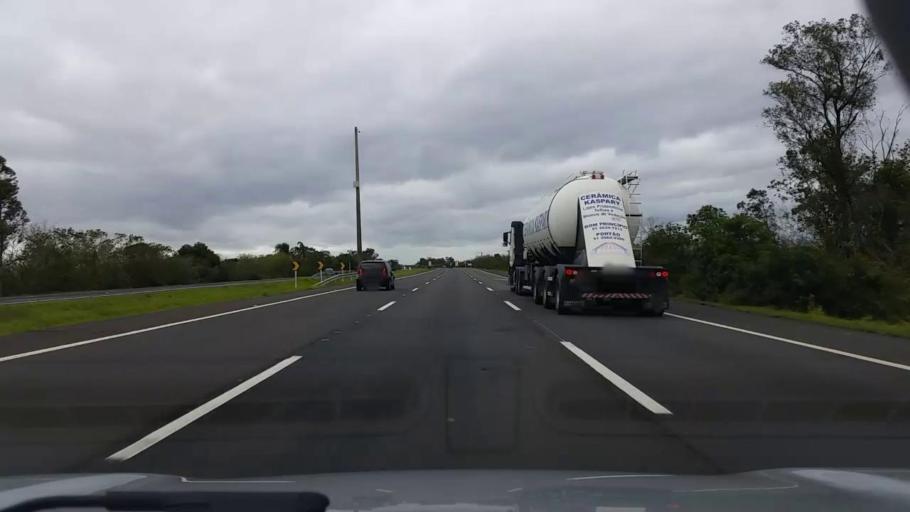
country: BR
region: Rio Grande do Sul
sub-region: Rolante
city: Rolante
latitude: -29.8838
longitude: -50.5606
